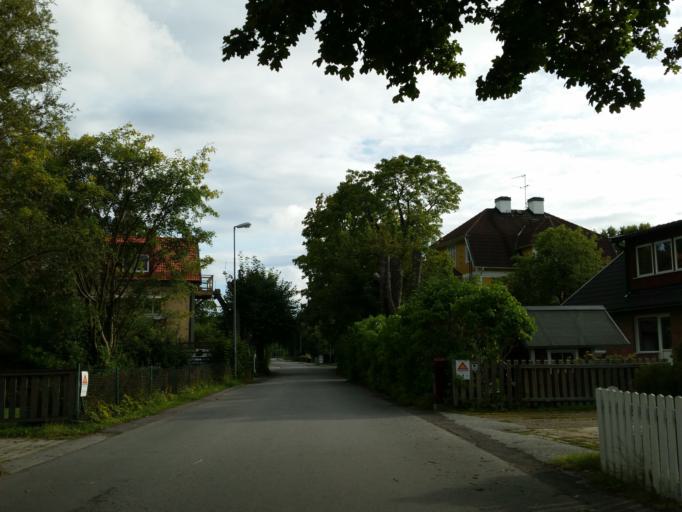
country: SE
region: Stockholm
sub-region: Sollentuna Kommun
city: Sollentuna
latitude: 59.4594
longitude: 17.9259
